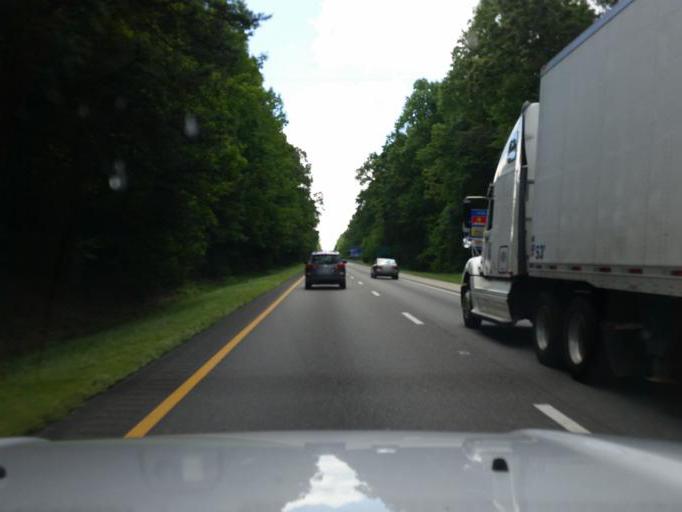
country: US
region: Virginia
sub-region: James City County
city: Williamsburg
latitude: 37.3626
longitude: -76.7428
